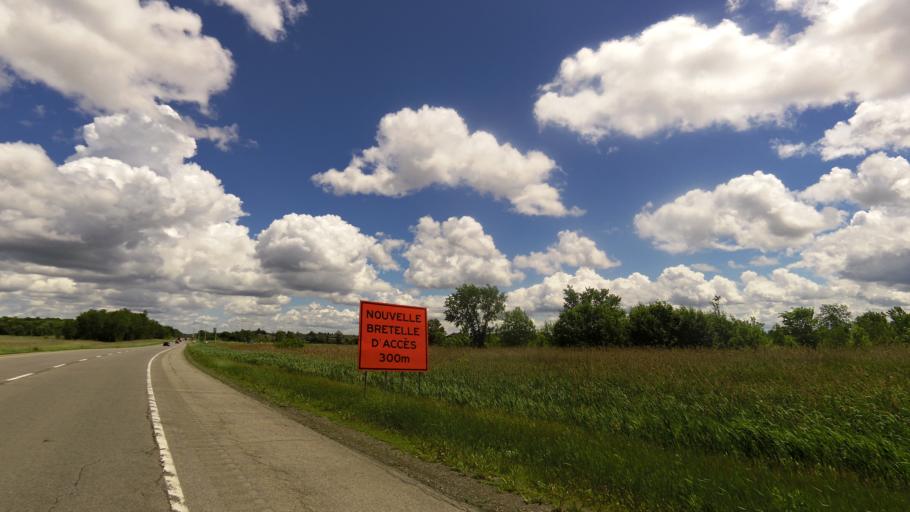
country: CA
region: Quebec
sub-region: Laurentides
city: Sainte-Marthe-sur-le-Lac
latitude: 45.5385
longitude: -73.9583
